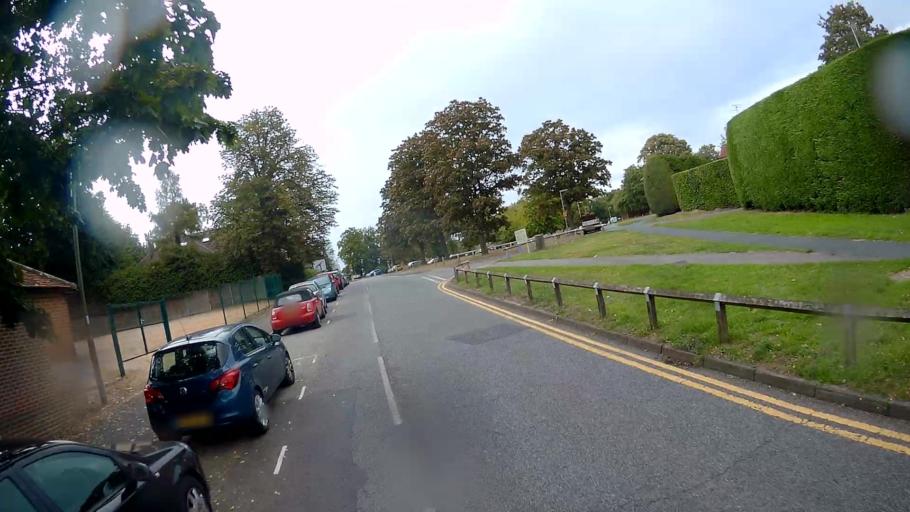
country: GB
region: England
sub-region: Surrey
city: Frimley
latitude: 51.3164
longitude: -0.7405
